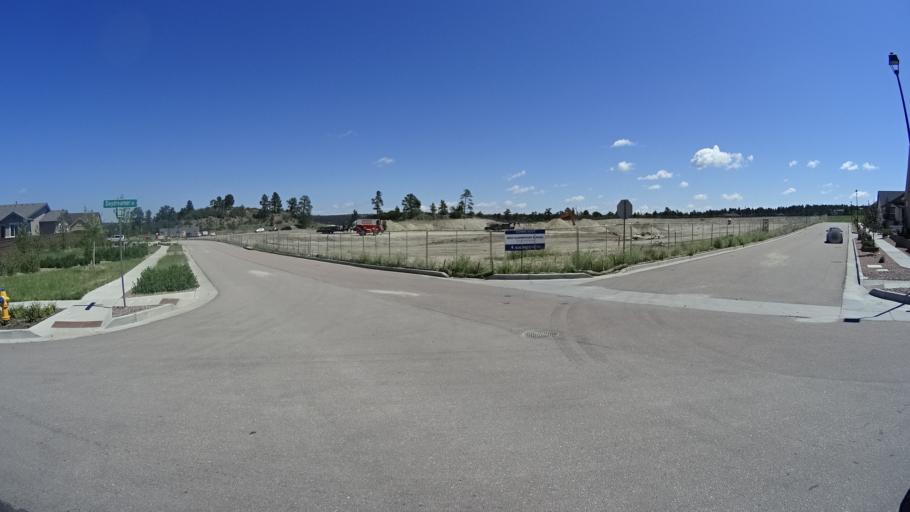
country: US
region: Colorado
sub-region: El Paso County
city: Black Forest
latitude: 38.9921
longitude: -104.7605
